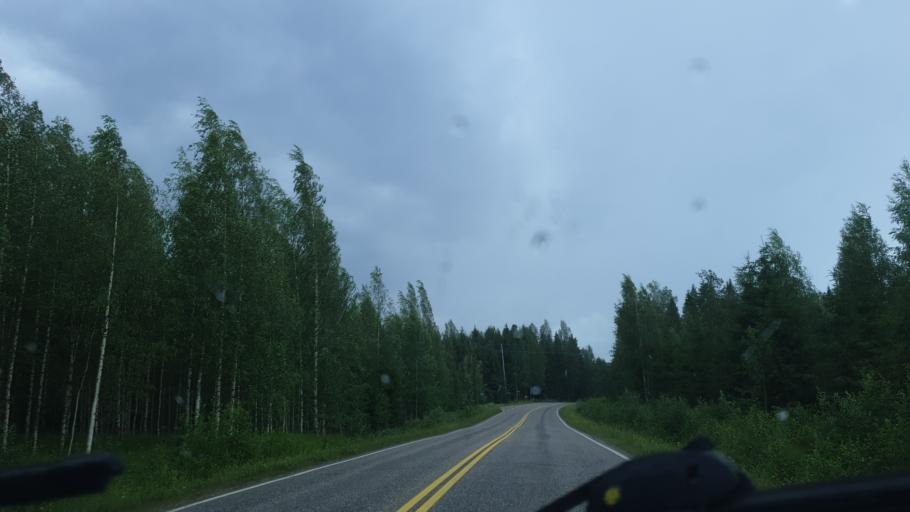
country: FI
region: Northern Savo
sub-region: Kuopio
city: Vehmersalmi
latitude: 62.9274
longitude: 27.9166
